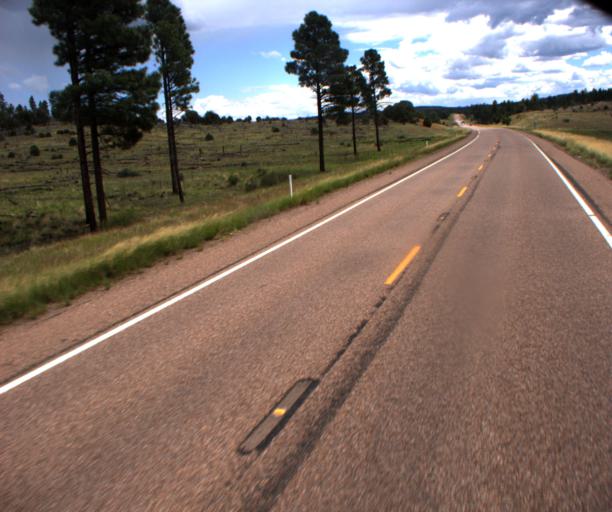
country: US
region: Arizona
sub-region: Navajo County
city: Linden
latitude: 34.3124
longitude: -110.2357
